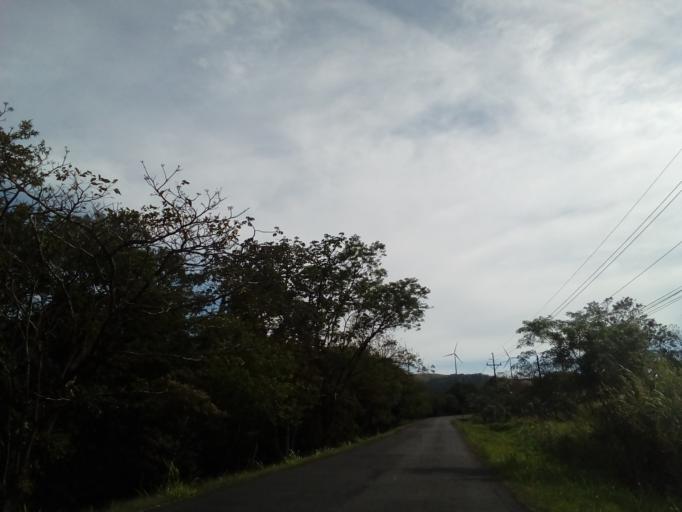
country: CR
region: Guanacaste
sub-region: Canton de Tilaran
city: Tilaran
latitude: 10.5507
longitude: -84.9745
